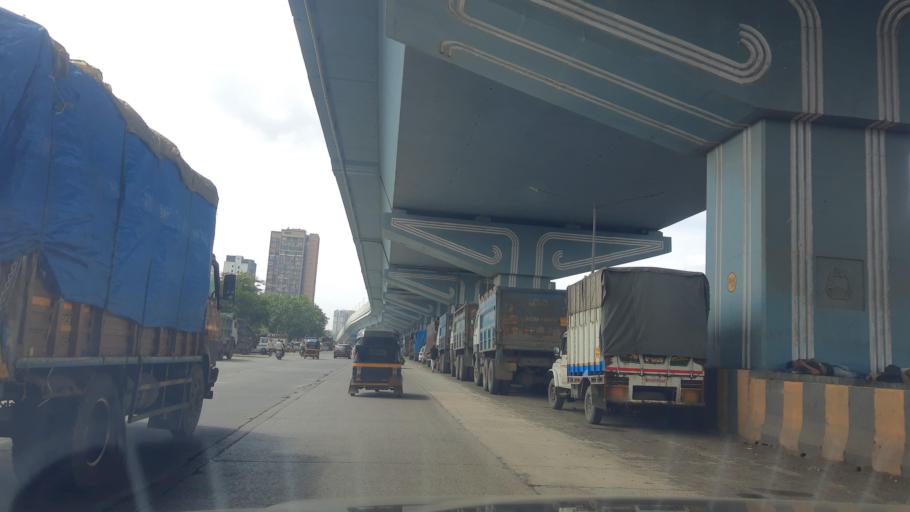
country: IN
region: Maharashtra
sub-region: Mumbai Suburban
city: Mumbai
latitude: 19.0602
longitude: 72.9219
